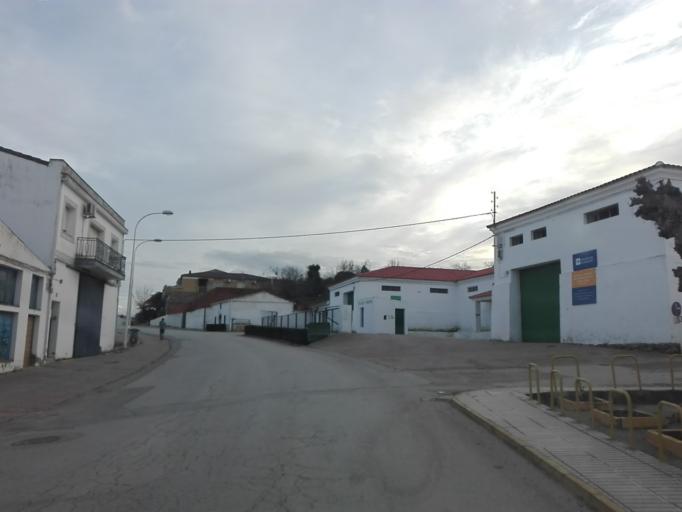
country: ES
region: Extremadura
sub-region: Provincia de Badajoz
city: Usagre
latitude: 38.3544
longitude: -6.1710
